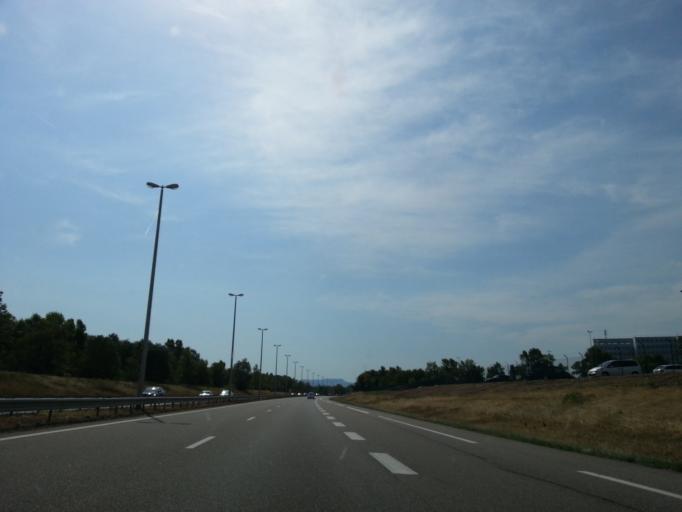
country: FR
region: Alsace
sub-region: Departement du Haut-Rhin
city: Saint-Louis
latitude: 47.5981
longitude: 7.5397
